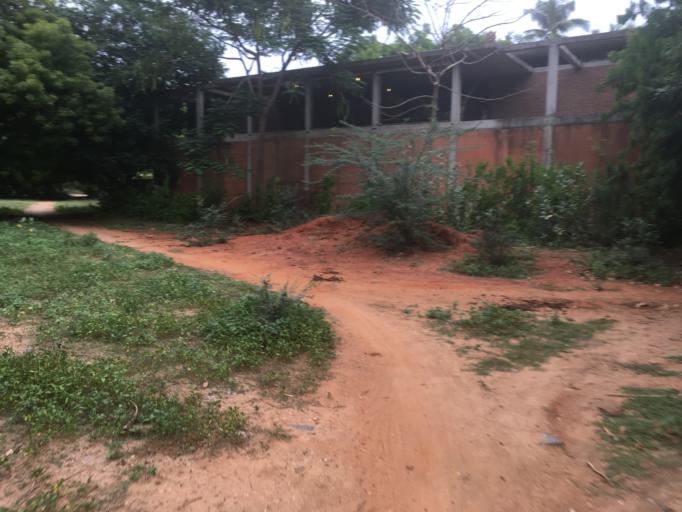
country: IN
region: Tamil Nadu
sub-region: Villupuram
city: Auroville
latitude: 12.0127
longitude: 79.8007
